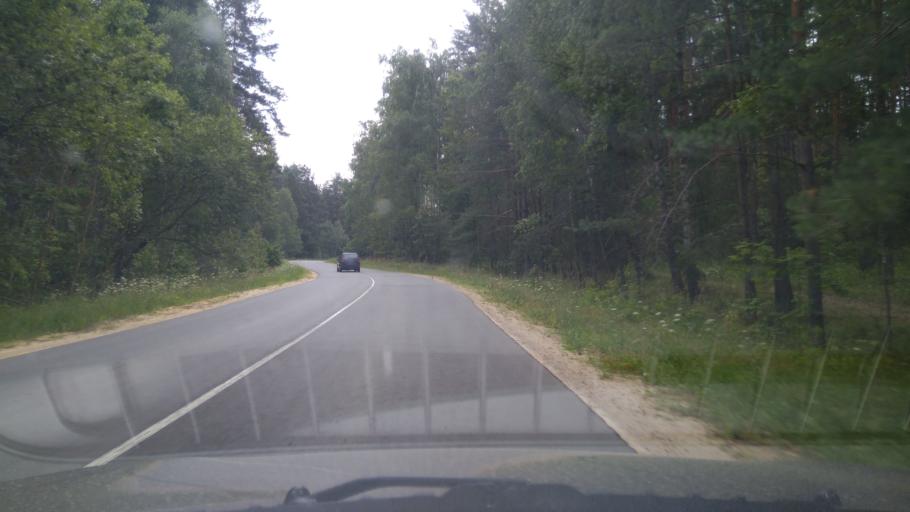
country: BY
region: Brest
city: Nyakhachava
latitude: 52.6025
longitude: 25.0889
